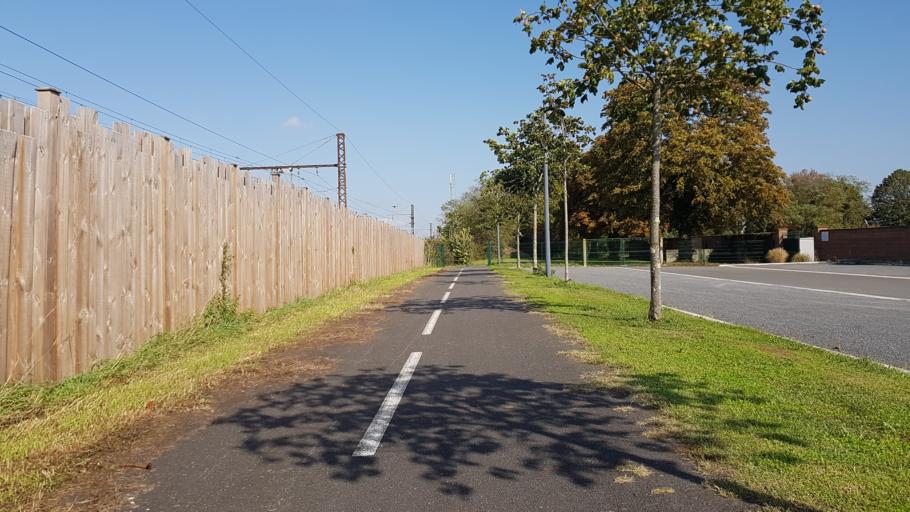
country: FR
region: Poitou-Charentes
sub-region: Departement de la Vienne
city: Chasseneuil-du-Poitou
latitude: 46.6535
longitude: 0.3744
